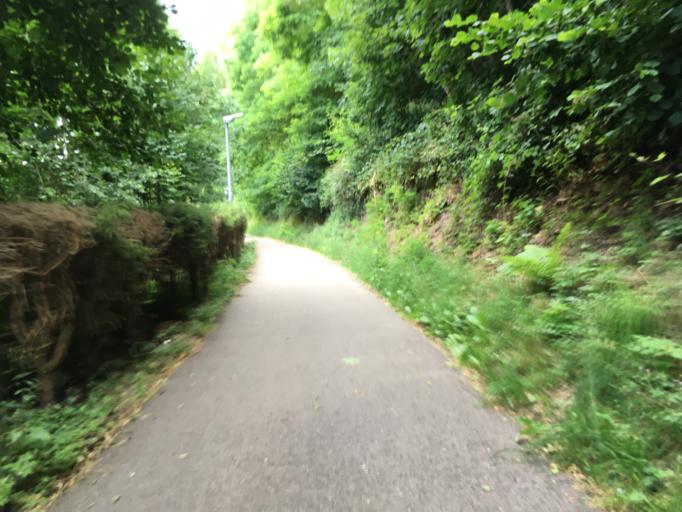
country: DE
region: Baden-Wuerttemberg
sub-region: Karlsruhe Region
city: Alpirsbach
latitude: 48.3425
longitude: 8.3959
